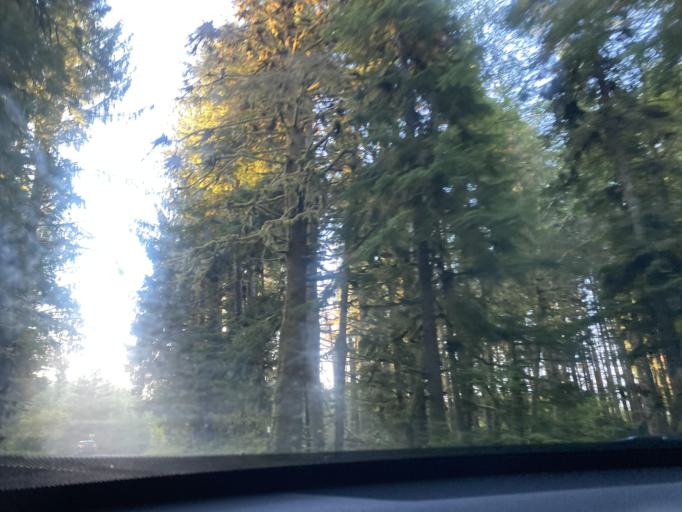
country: US
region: Washington
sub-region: Clallam County
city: Forks
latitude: 47.8100
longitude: -124.1030
